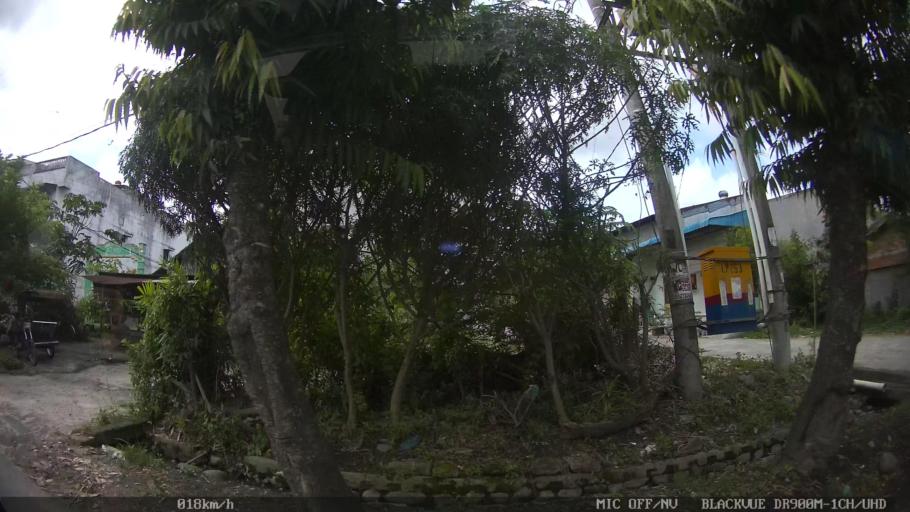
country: ID
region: North Sumatra
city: Percut
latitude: 3.5667
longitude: 98.8745
